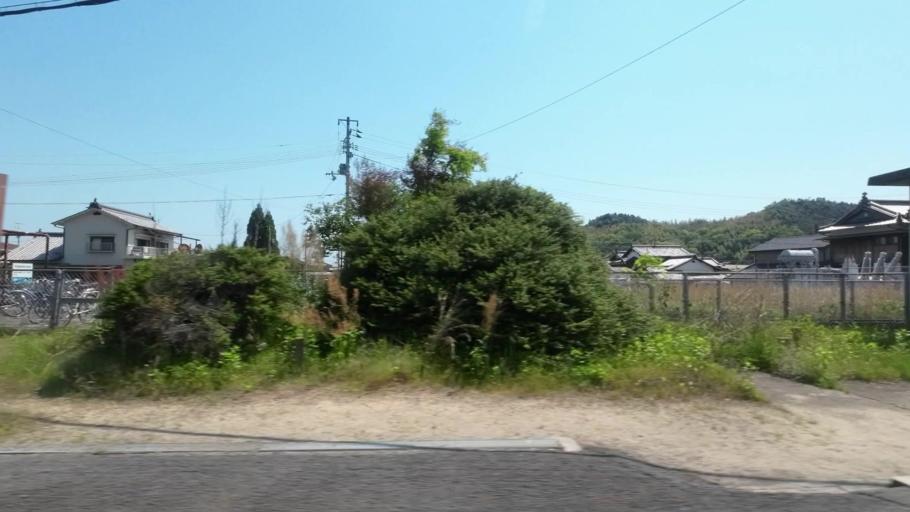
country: JP
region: Ehime
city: Saijo
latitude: 34.0120
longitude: 133.0358
